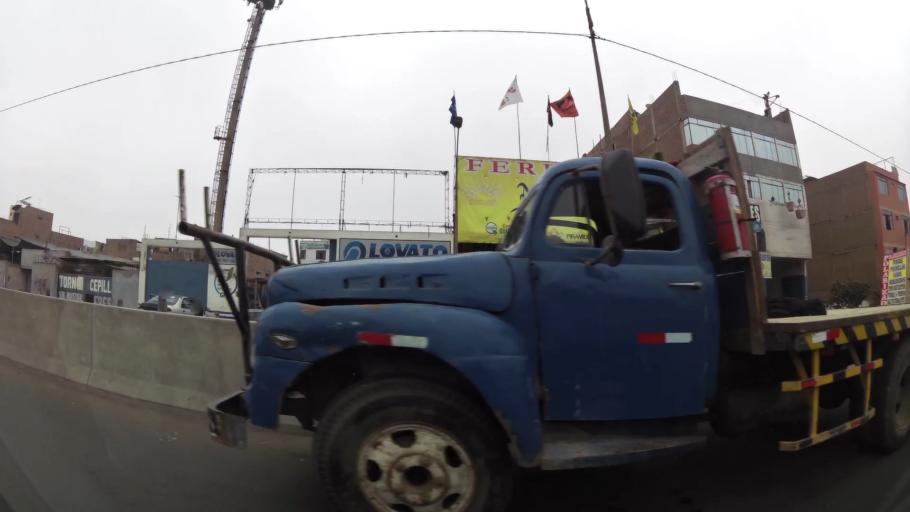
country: PE
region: Lima
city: Ventanilla
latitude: -11.8529
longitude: -77.0895
